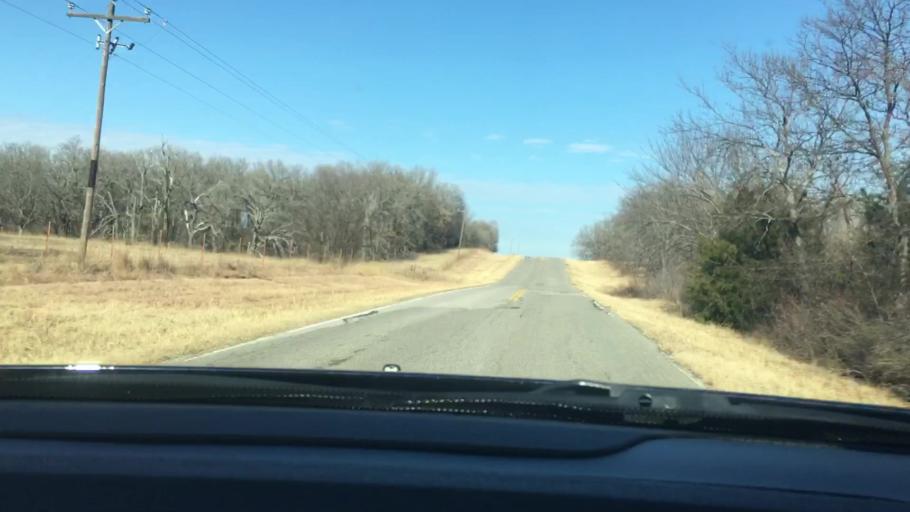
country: US
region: Oklahoma
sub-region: Garvin County
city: Wynnewood
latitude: 34.6689
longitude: -97.1254
